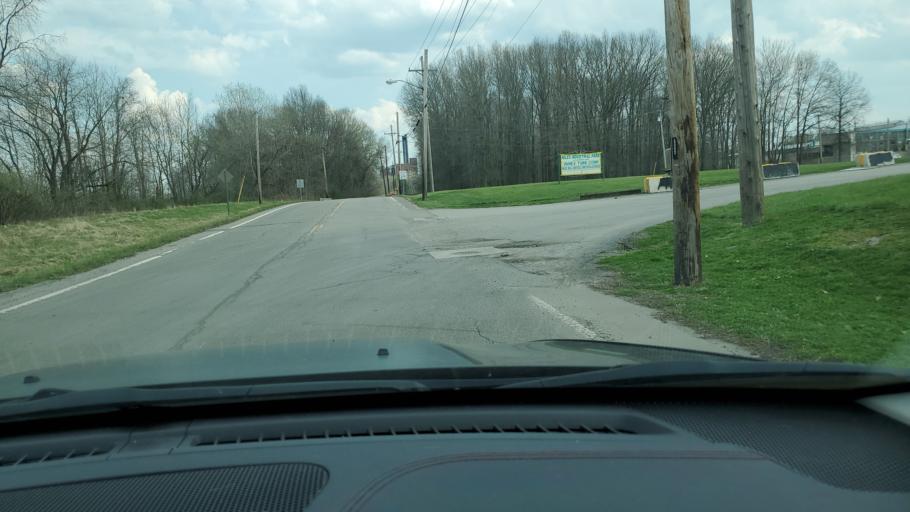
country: US
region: Ohio
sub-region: Trumbull County
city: Niles
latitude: 41.1689
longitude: -80.7601
